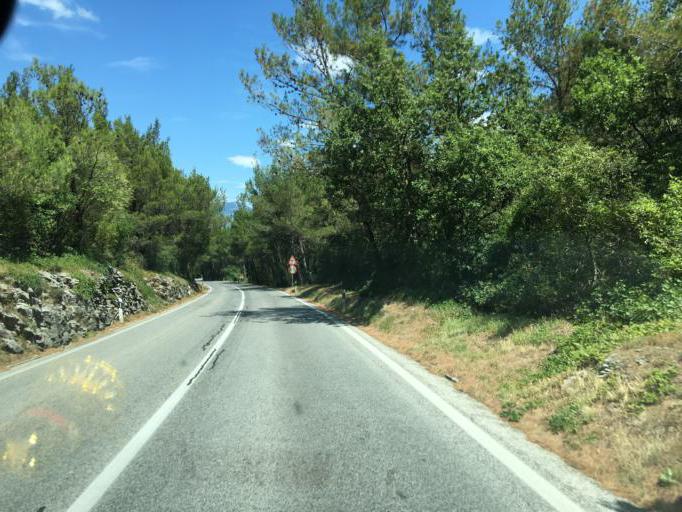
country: HR
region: Istarska
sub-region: Grad Labin
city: Labin
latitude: 45.1506
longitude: 14.1556
